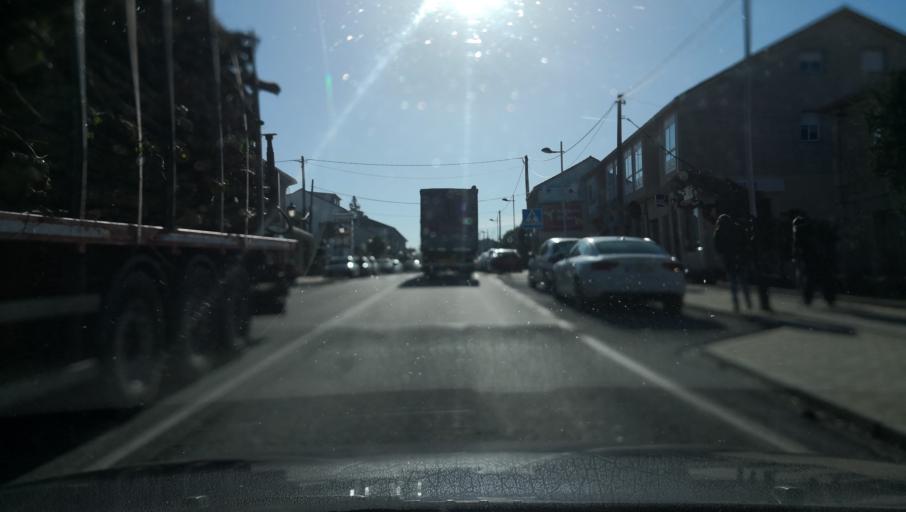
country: ES
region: Galicia
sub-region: Provincia da Coruna
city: Vedra
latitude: 42.7982
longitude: -8.4706
